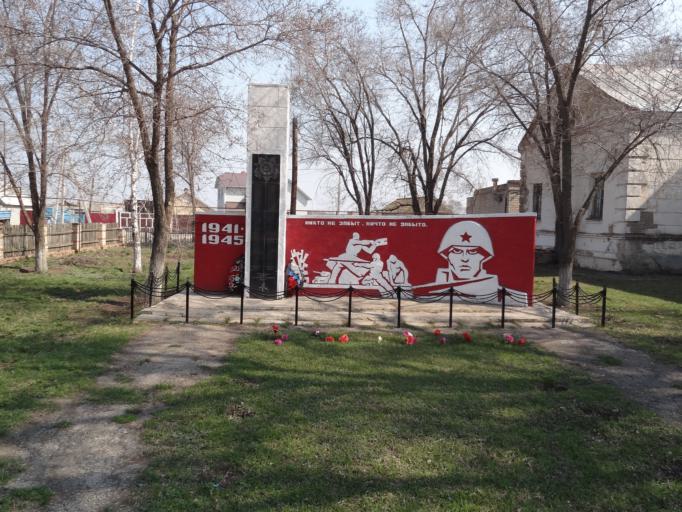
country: RU
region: Saratov
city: Privolzhskiy
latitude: 51.3049
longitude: 45.9603
